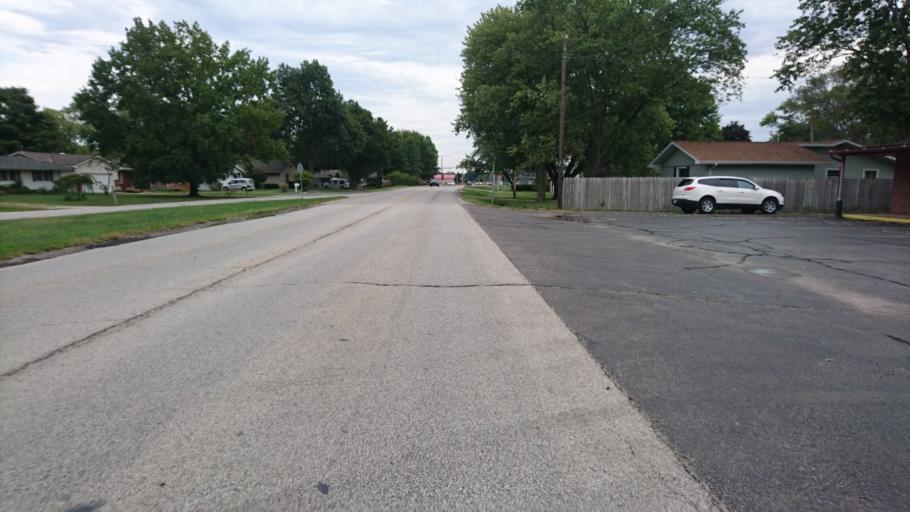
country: US
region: Illinois
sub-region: Sangamon County
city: Chatham
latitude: 39.6764
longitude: -89.6982
